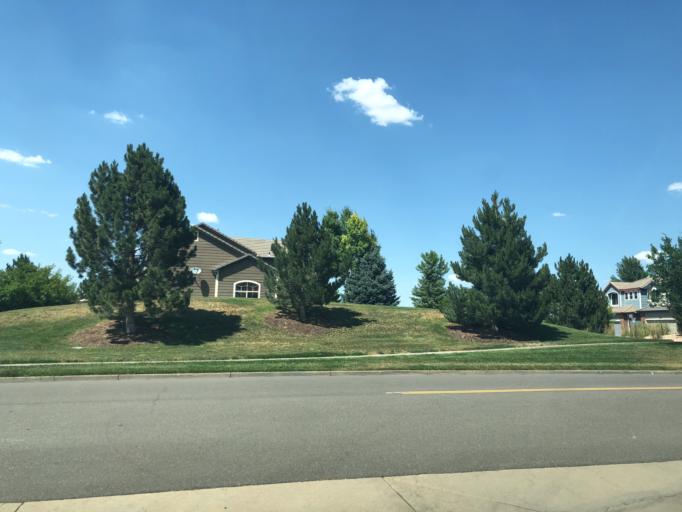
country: US
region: Colorado
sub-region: Arapahoe County
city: Dove Valley
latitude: 39.6025
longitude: -104.7830
